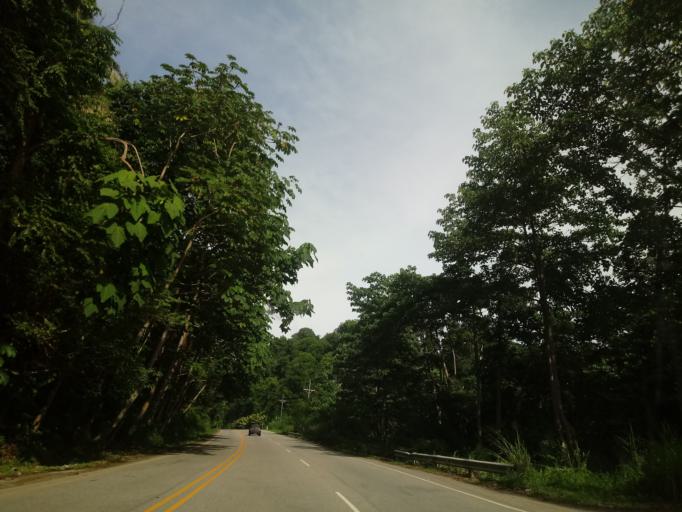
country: CR
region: San Jose
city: Daniel Flores
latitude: 9.2012
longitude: -83.7908
